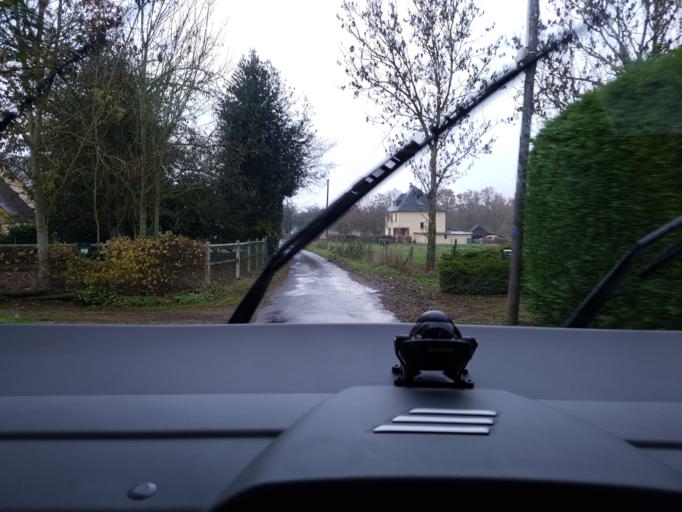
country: FR
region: Haute-Normandie
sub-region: Departement de l'Eure
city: Beuzeville
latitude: 49.3954
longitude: 0.3963
